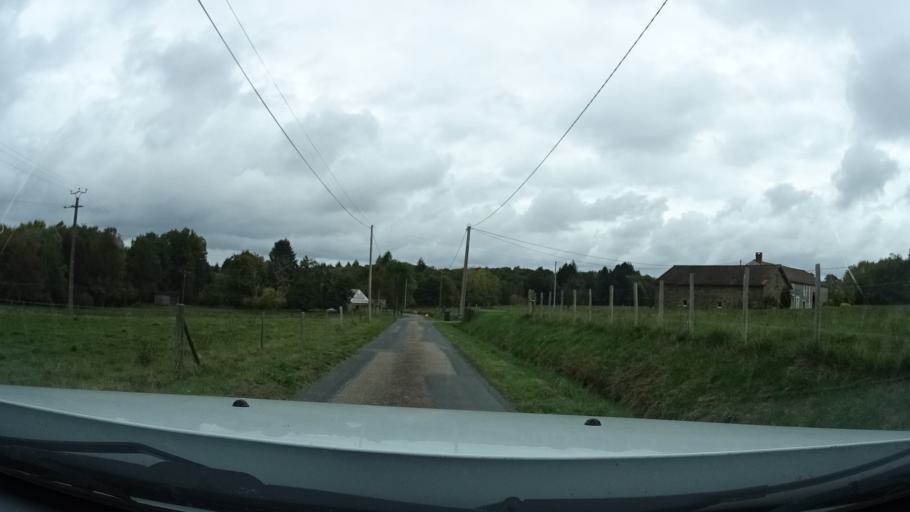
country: FR
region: Aquitaine
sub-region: Departement de la Dordogne
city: La Coquille
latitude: 45.5437
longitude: 0.9185
